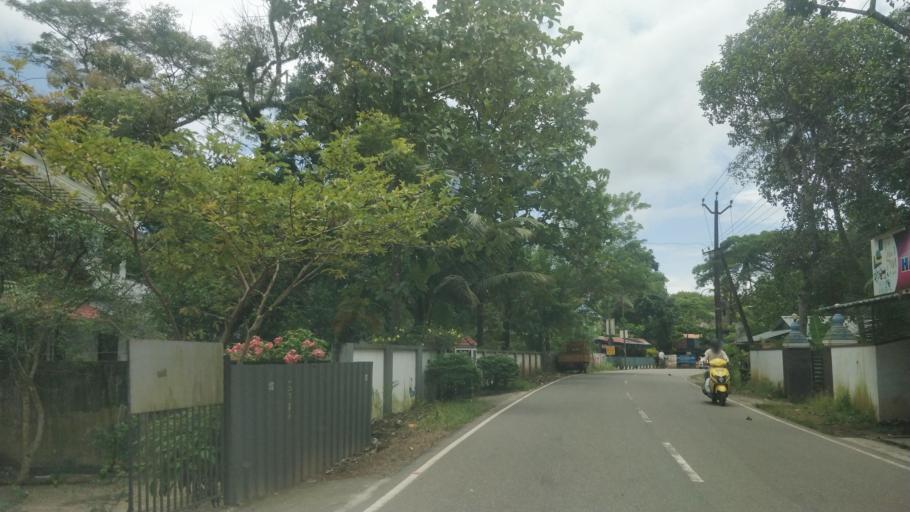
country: IN
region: Kerala
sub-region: Alappuzha
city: Shertallai
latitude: 9.6577
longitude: 76.3622
